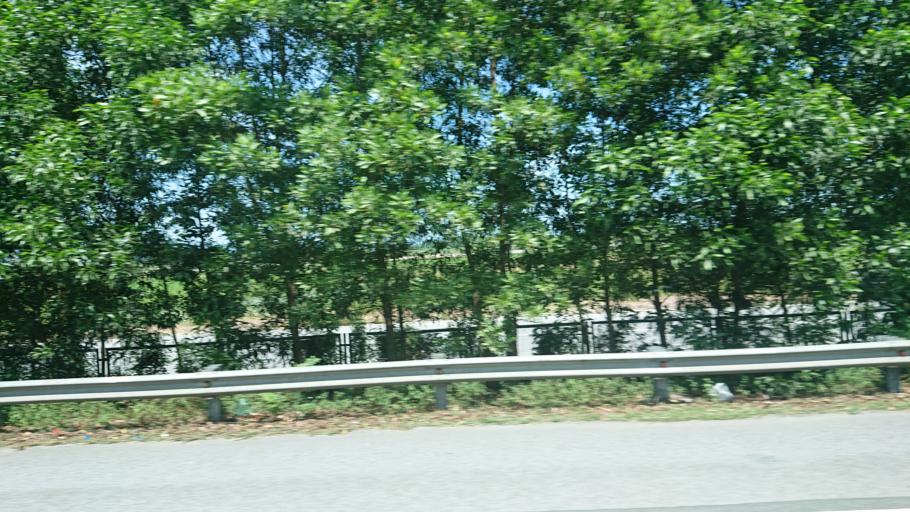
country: VN
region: Ha Nam
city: Thi Tran Hoa Mac
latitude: 20.5971
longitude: 105.9490
